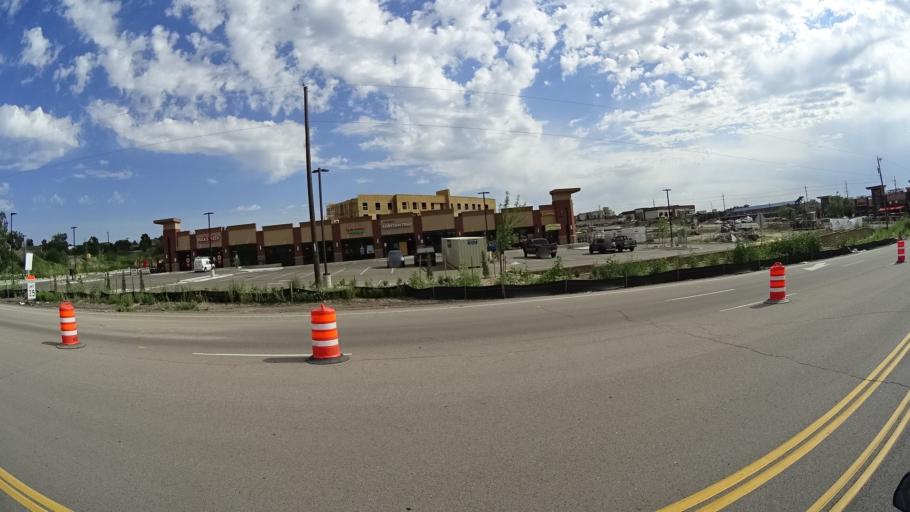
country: US
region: Colorado
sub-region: El Paso County
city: Cimarron Hills
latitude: 38.8941
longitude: -104.7227
